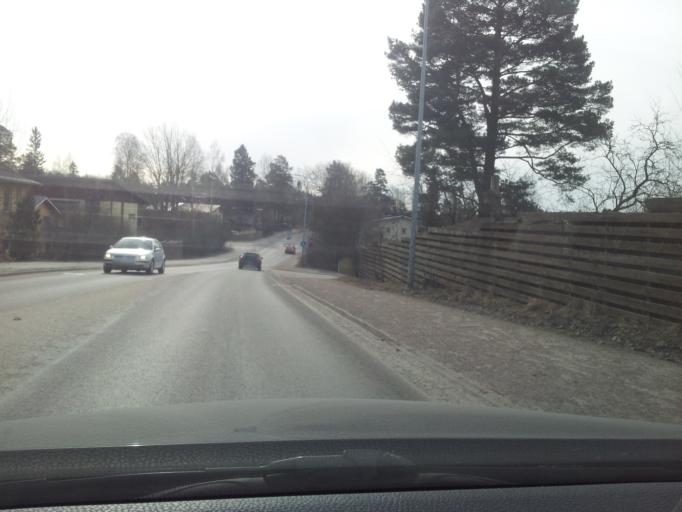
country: FI
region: Uusimaa
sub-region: Helsinki
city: Kilo
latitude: 60.1863
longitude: 24.7850
